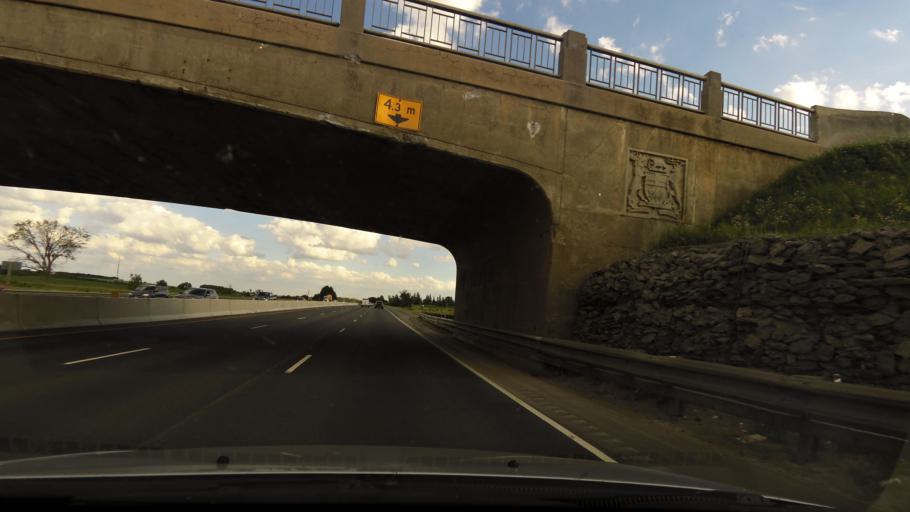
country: CA
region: Ontario
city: Bradford West Gwillimbury
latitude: 44.0749
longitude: -79.6249
